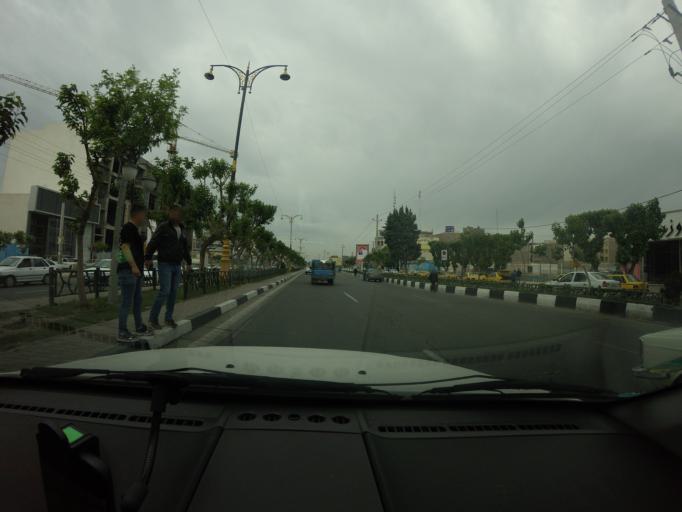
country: IR
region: Tehran
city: Eslamshahr
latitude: 35.5575
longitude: 51.2432
